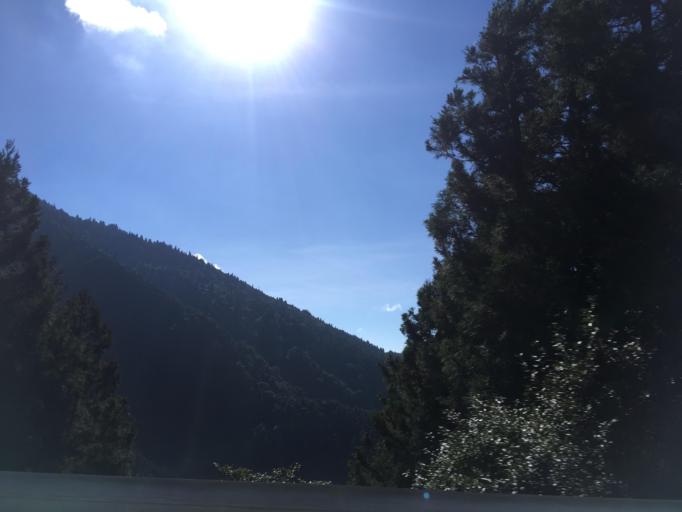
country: TW
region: Taiwan
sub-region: Yilan
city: Yilan
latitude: 24.5024
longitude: 121.5536
